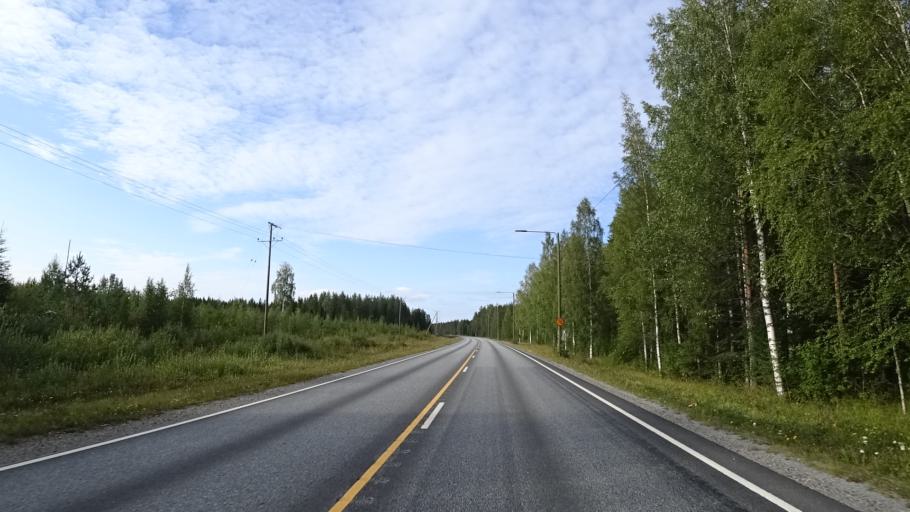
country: FI
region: North Karelia
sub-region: Joensuu
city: Eno
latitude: 62.8677
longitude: 30.2012
